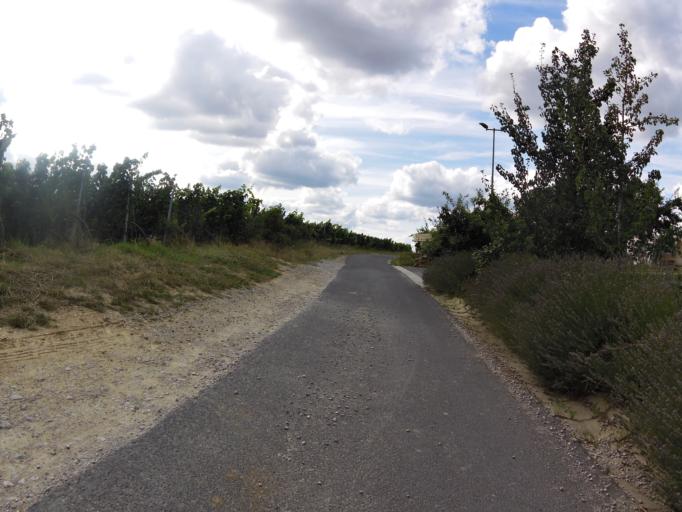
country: DE
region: Bavaria
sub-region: Regierungsbezirk Unterfranken
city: Sommerhausen
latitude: 49.6980
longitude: 10.0363
